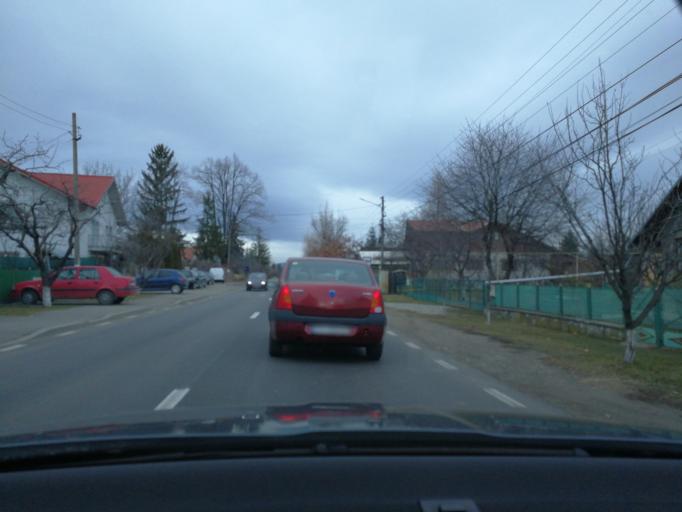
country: RO
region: Prahova
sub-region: Oras Breaza
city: Breaza de Jos
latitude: 45.1630
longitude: 25.6844
